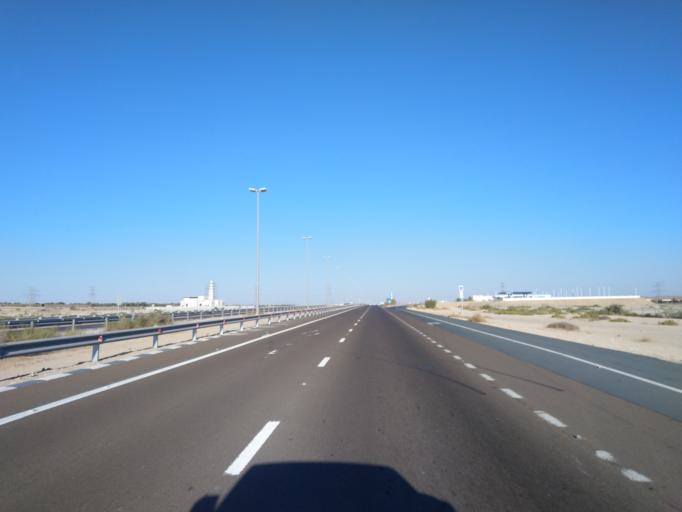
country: OM
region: Al Buraimi
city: Al Buraymi
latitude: 24.5184
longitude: 55.5111
